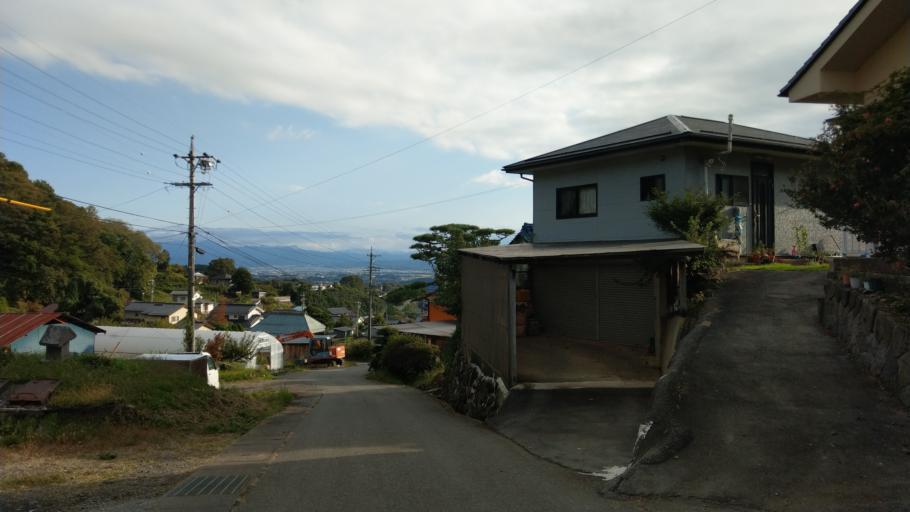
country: JP
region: Nagano
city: Komoro
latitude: 36.3555
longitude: 138.4313
